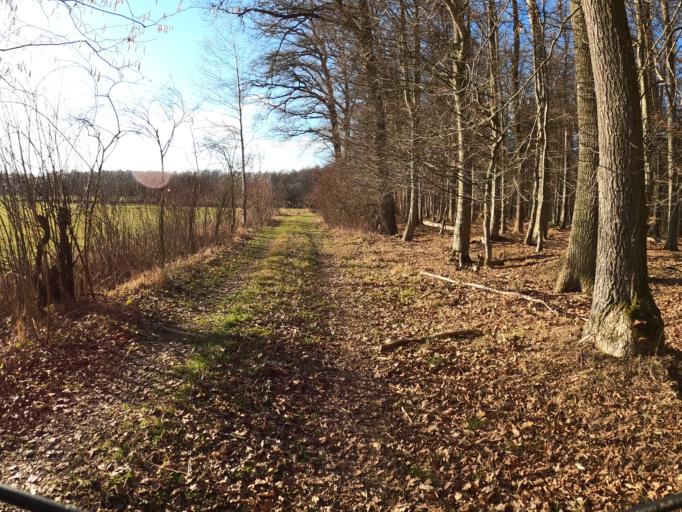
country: DE
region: Bavaria
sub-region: Swabia
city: Bubesheim
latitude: 48.4192
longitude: 10.2247
